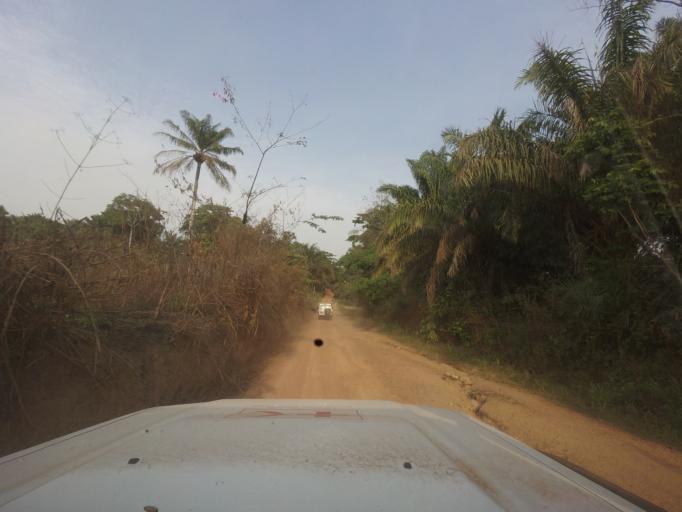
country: GN
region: Nzerekore
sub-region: Prefecture de Guekedou
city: Gueckedou
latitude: 8.5238
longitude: -10.1869
